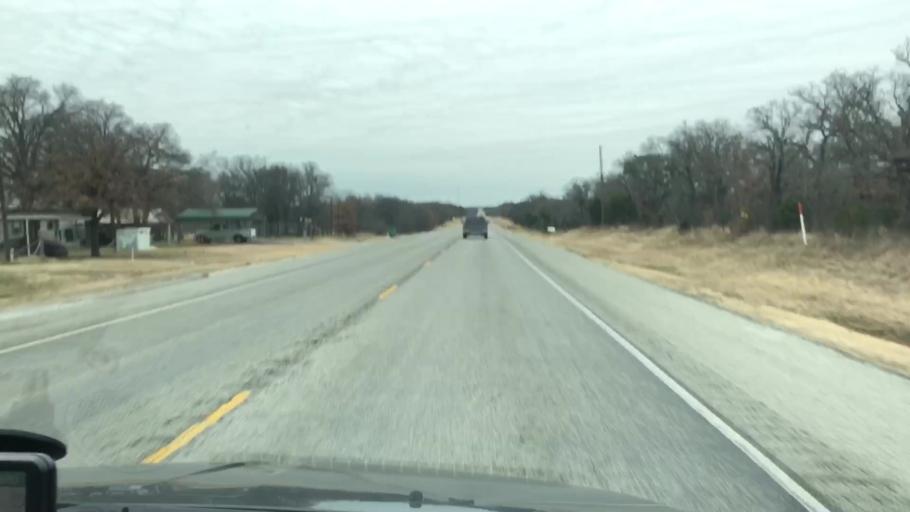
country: US
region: Texas
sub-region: Palo Pinto County
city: Mineral Wells
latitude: 32.8935
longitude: -98.0867
